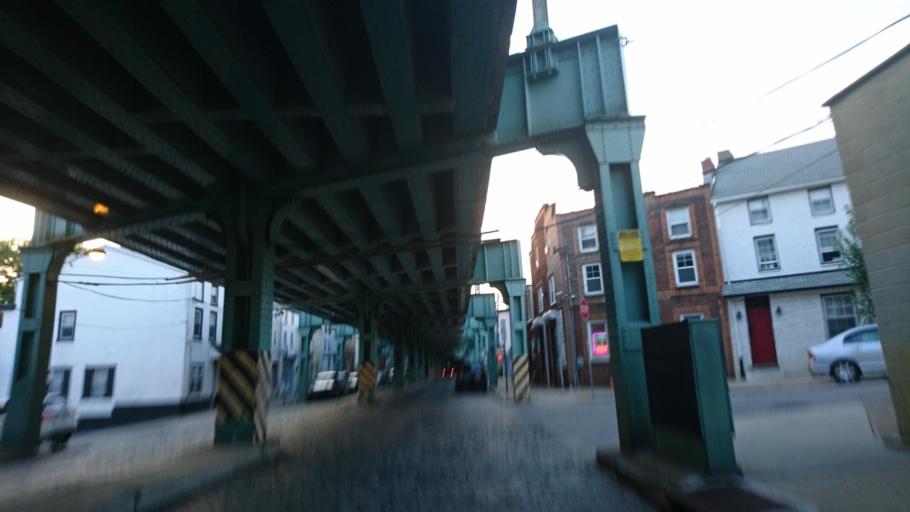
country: US
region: Pennsylvania
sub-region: Montgomery County
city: Bala-Cynwyd
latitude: 40.0260
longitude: -75.2227
